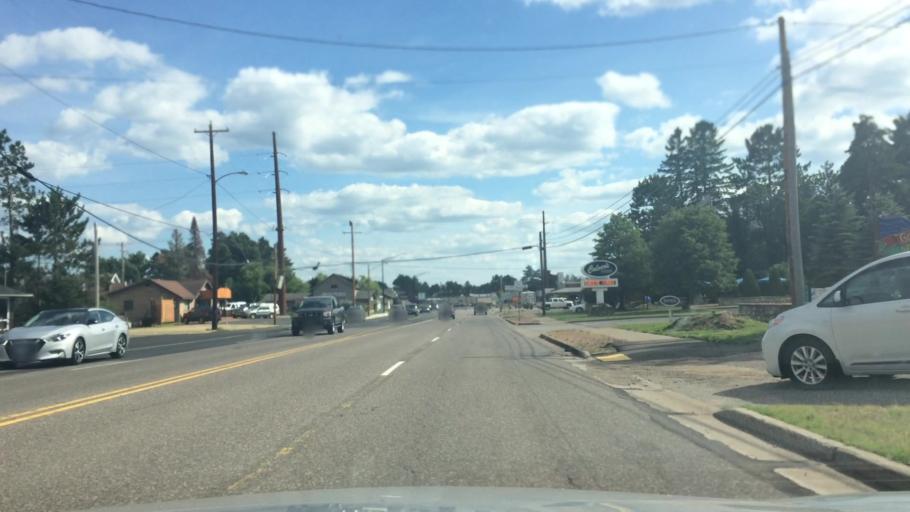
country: US
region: Wisconsin
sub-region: Vilas County
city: Lac du Flambeau
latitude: 45.8999
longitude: -89.6975
